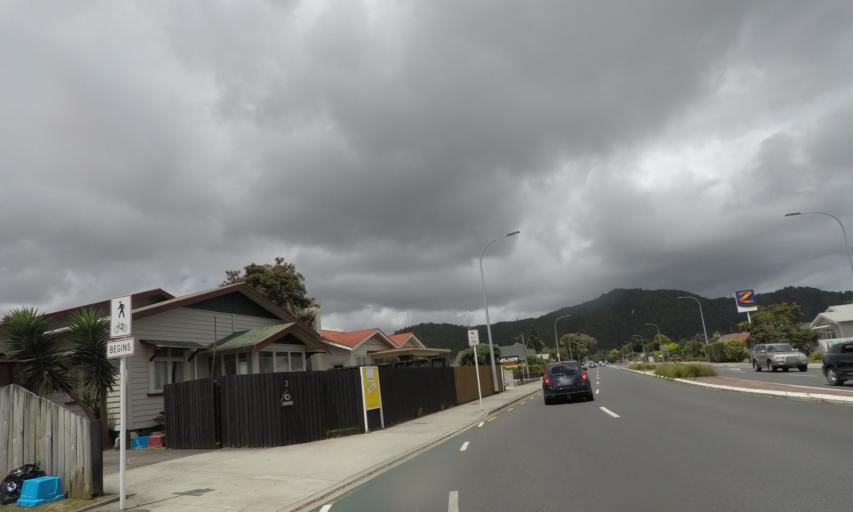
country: NZ
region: Northland
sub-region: Whangarei
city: Whangarei
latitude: -35.7082
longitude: 174.3219
